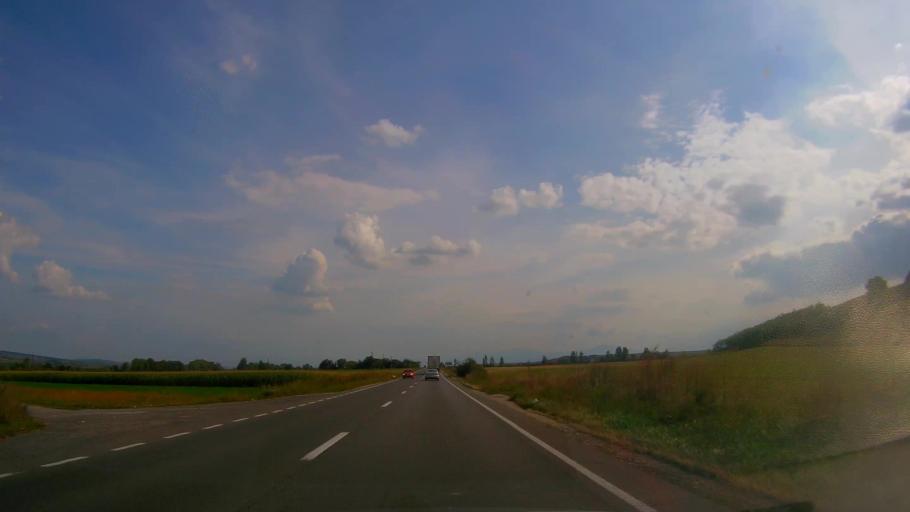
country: RO
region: Brasov
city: Maierus
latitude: 45.8739
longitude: 25.5407
